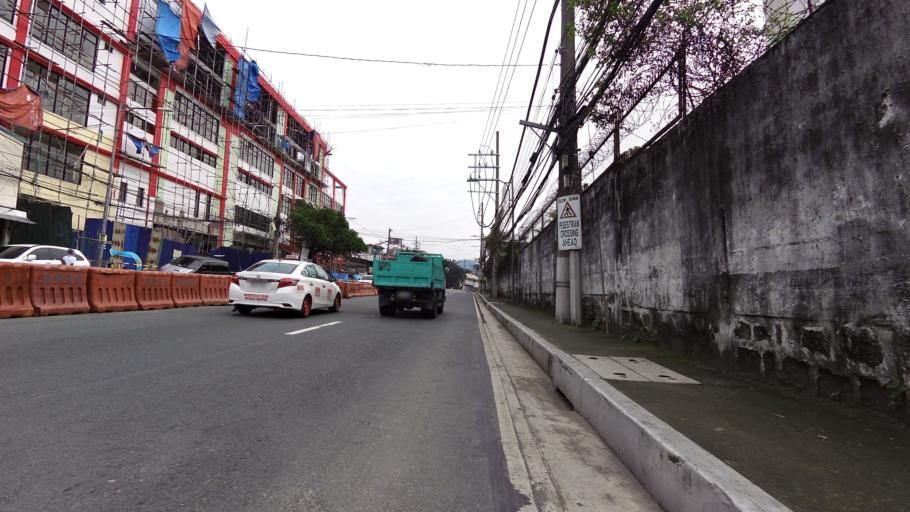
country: PH
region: Metro Manila
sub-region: San Juan
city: San Juan
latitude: 14.6081
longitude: 121.0400
